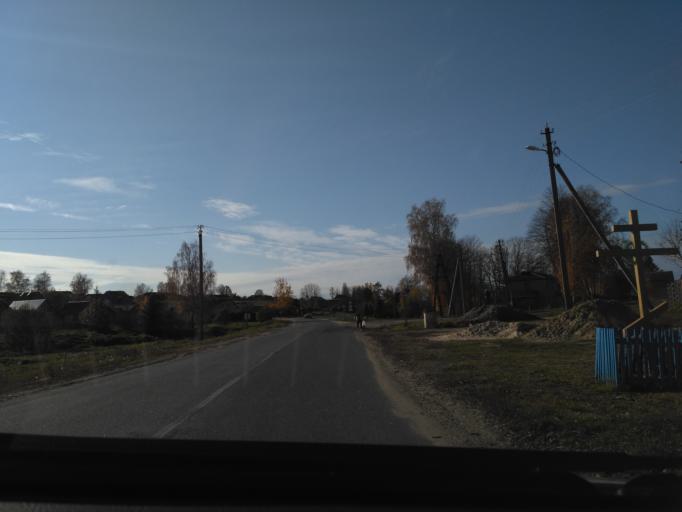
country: BY
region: Minsk
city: Loshnitsa
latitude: 54.3618
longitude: 28.6252
